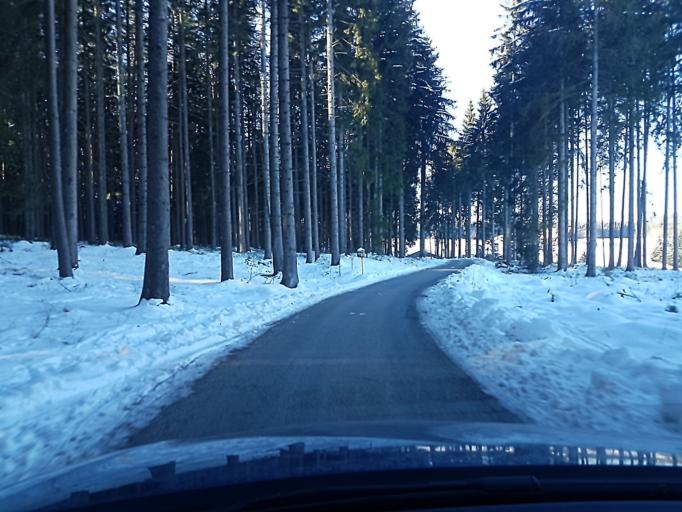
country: DE
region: Baden-Wuerttemberg
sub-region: Freiburg Region
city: Unterkirnach
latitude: 48.0824
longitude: 8.3670
